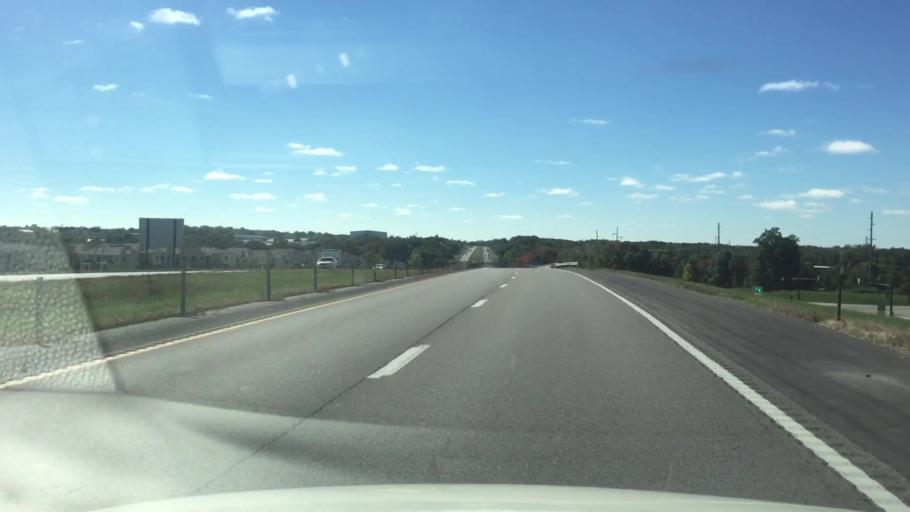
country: US
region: Missouri
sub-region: Boone County
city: Columbia
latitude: 38.9337
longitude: -92.2952
